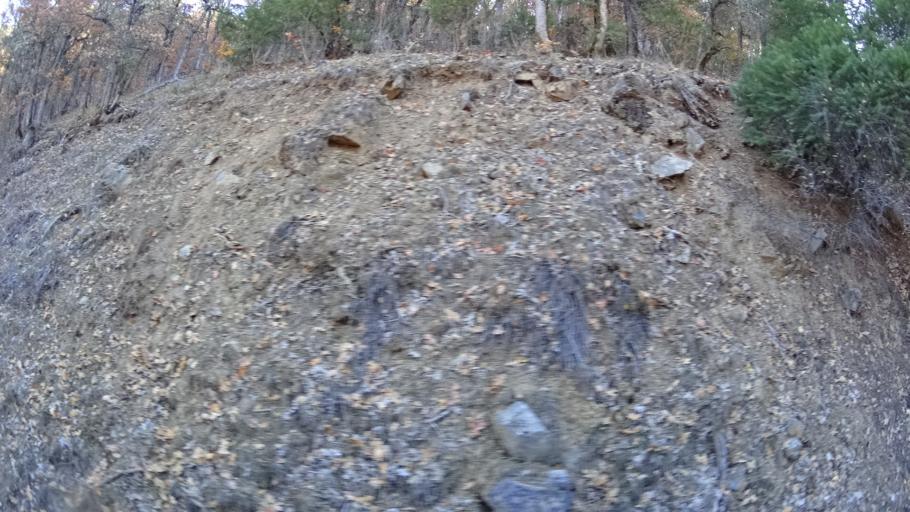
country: US
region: California
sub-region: Siskiyou County
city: Yreka
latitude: 41.8598
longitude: -122.7460
